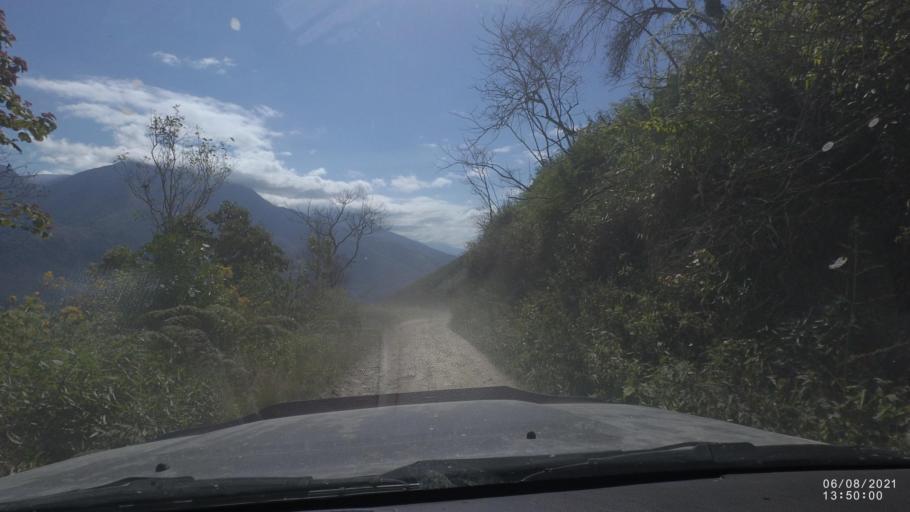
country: BO
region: La Paz
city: Quime
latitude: -16.6586
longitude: -66.7227
